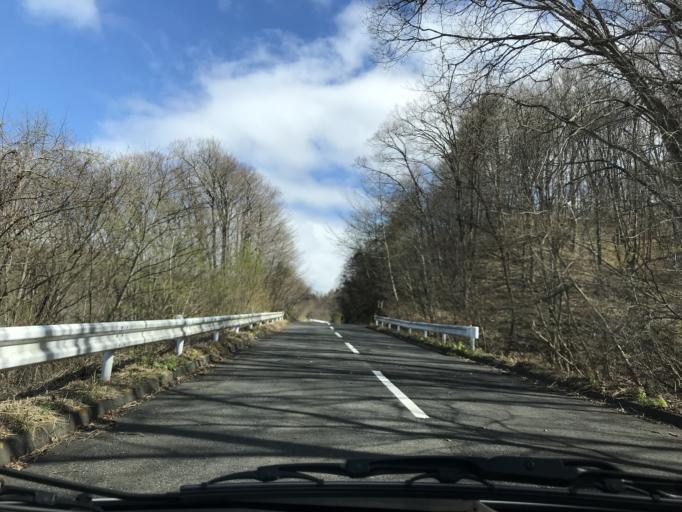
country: JP
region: Iwate
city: Mizusawa
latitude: 39.0725
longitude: 140.9849
